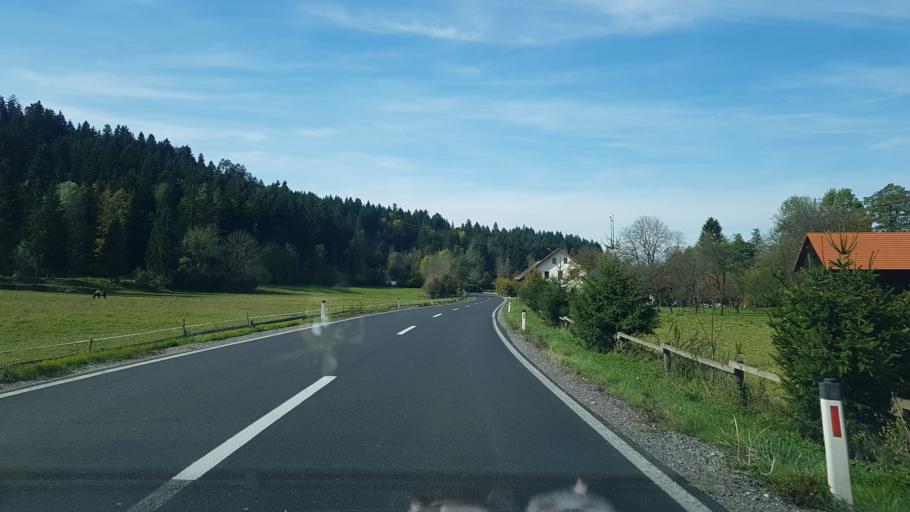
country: SI
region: Slovenj Gradec
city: Legen
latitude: 46.4490
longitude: 15.1628
